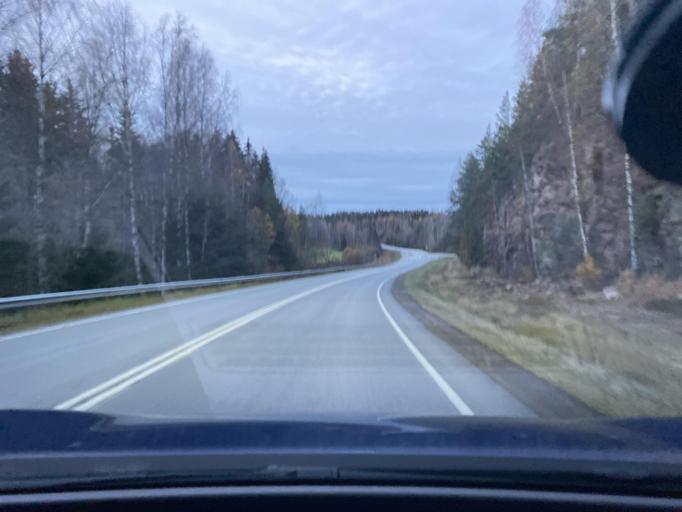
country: FI
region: Uusimaa
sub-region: Helsinki
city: Sammatti
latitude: 60.3887
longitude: 23.8146
